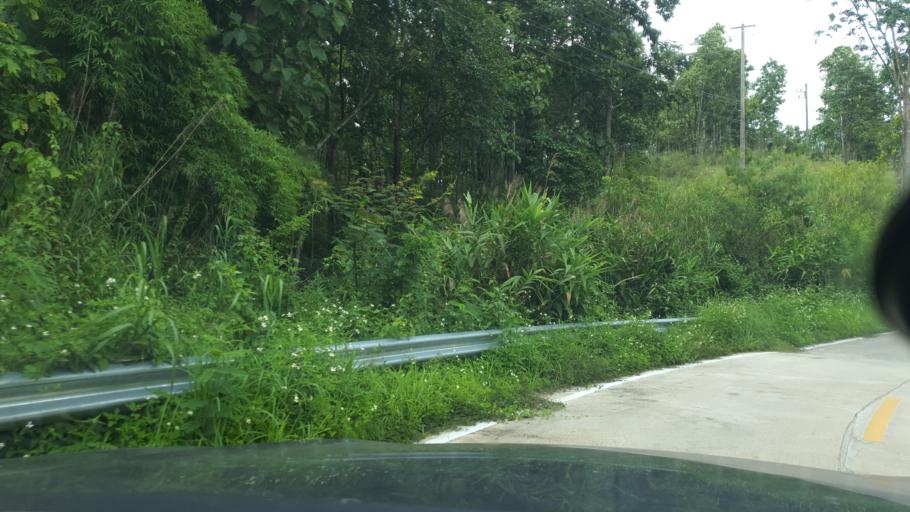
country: TH
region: Lamphun
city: Mae Tha
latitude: 18.5115
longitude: 99.2628
